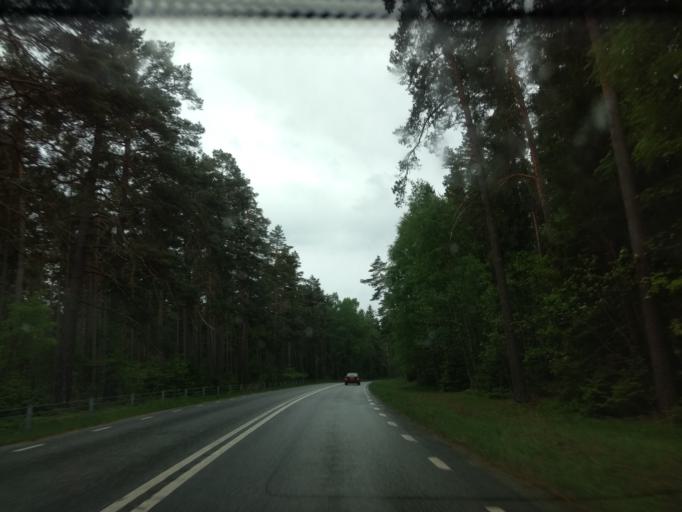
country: SE
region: Uppsala
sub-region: Uppsala Kommun
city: Saevja
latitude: 59.7754
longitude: 17.6617
